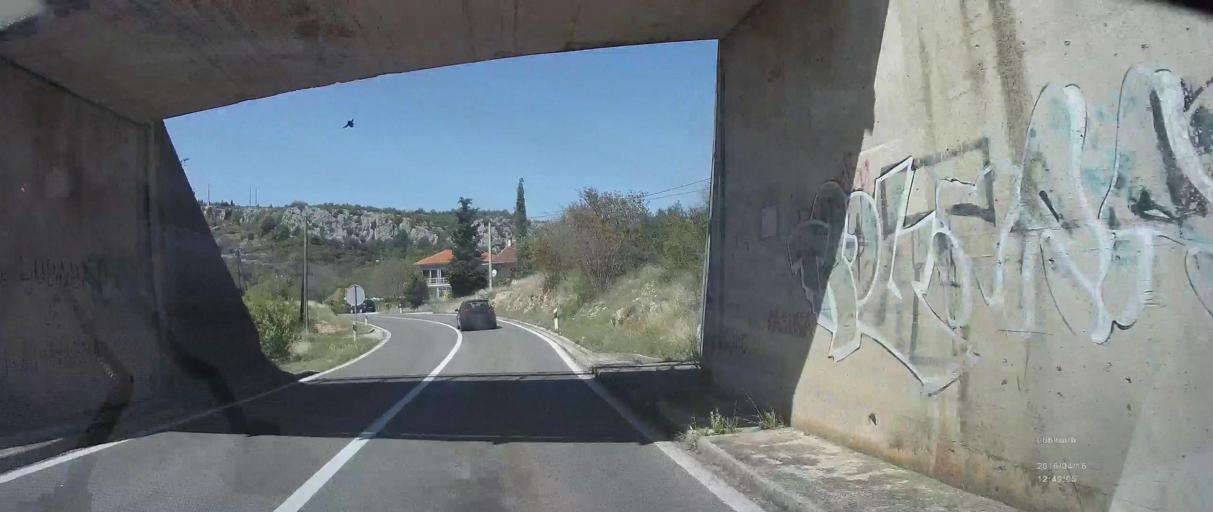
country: HR
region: Sibensko-Kniniska
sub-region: Grad Sibenik
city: Brodarica
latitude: 43.6732
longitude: 16.0299
